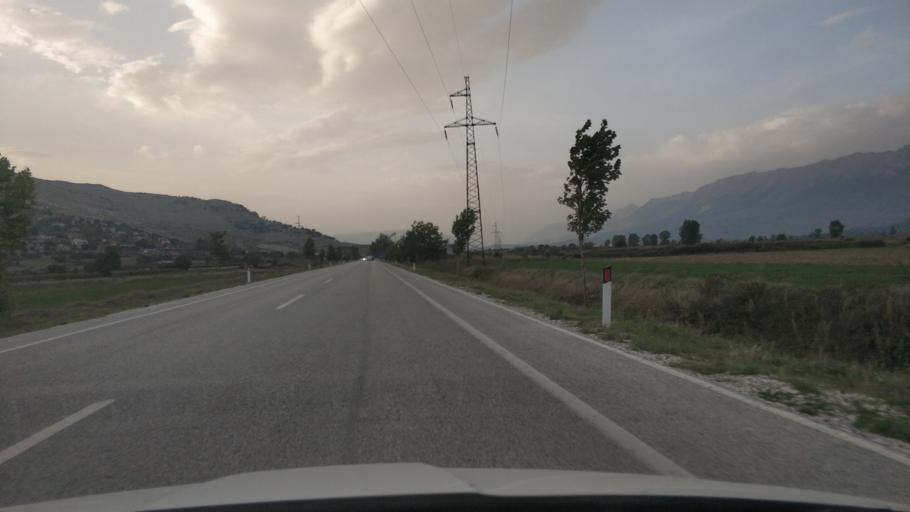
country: AL
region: Gjirokaster
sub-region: Rrethi i Gjirokastres
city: Libohove
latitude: 39.9604
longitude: 20.2456
